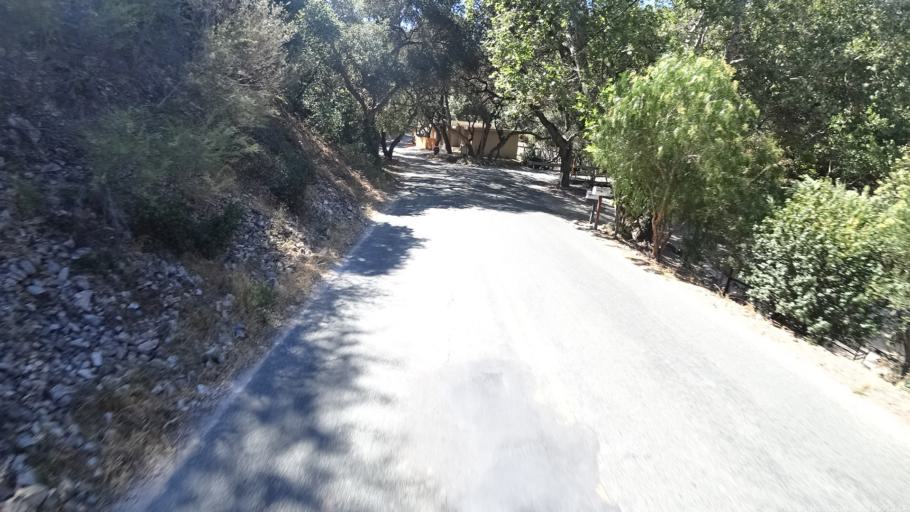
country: US
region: California
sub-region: Monterey County
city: Carmel Valley Village
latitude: 36.4713
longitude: -121.7242
